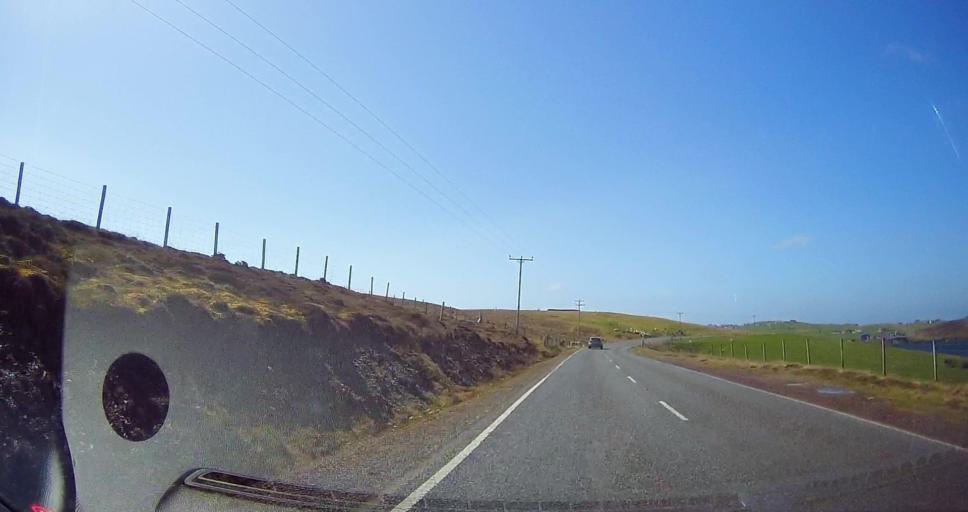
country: GB
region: Scotland
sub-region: Shetland Islands
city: Sandwick
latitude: 60.1083
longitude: -1.2969
